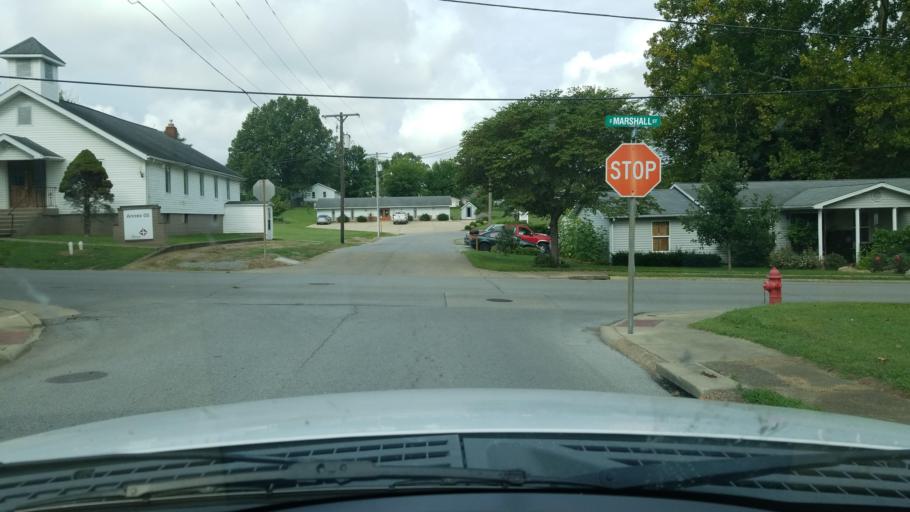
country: US
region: Illinois
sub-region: Saline County
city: Harrisburg
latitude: 37.7303
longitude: -88.5263
